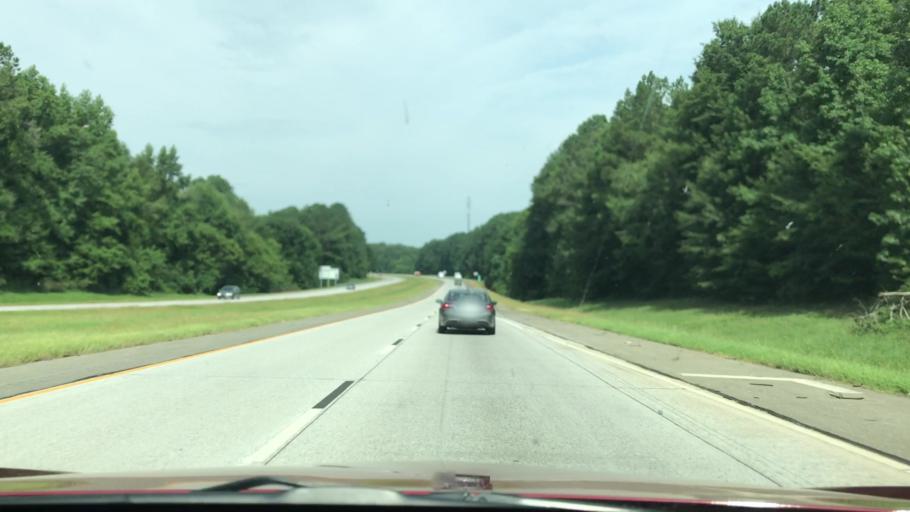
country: US
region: Georgia
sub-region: Morgan County
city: Madison
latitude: 33.5538
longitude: -83.3667
